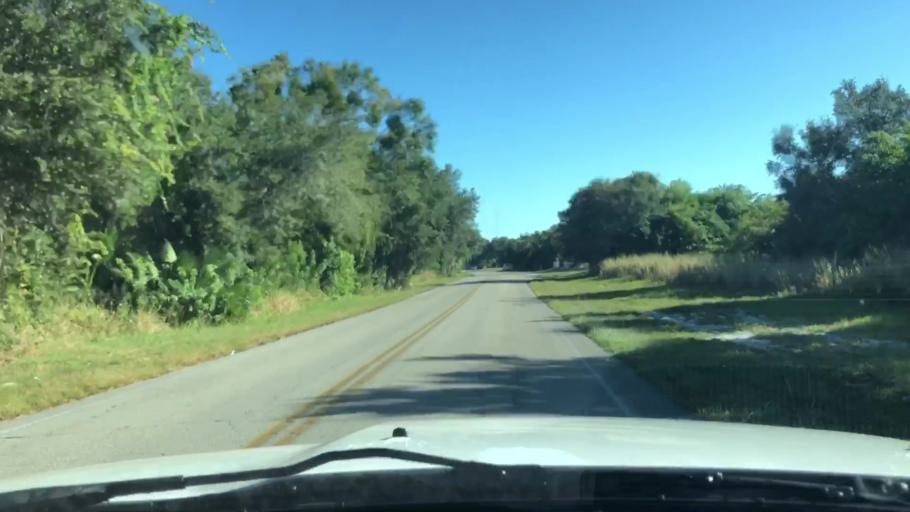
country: US
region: Florida
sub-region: Indian River County
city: Florida Ridge
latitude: 27.5691
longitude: -80.3738
